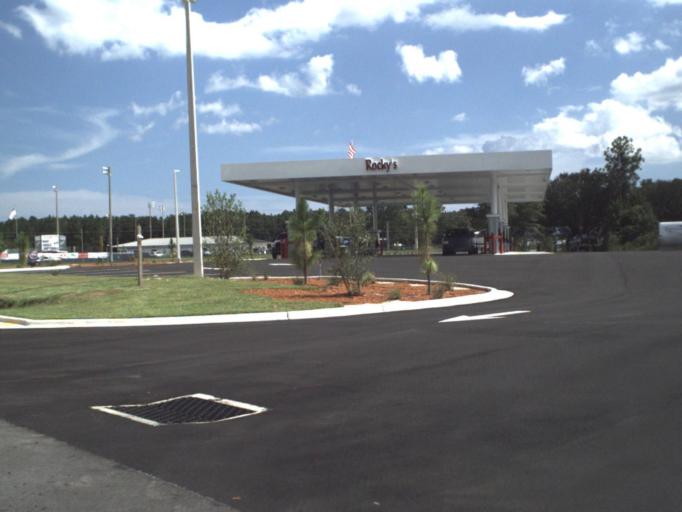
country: US
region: Florida
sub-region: Wakulla County
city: Crawfordville
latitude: 30.1077
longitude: -84.3801
